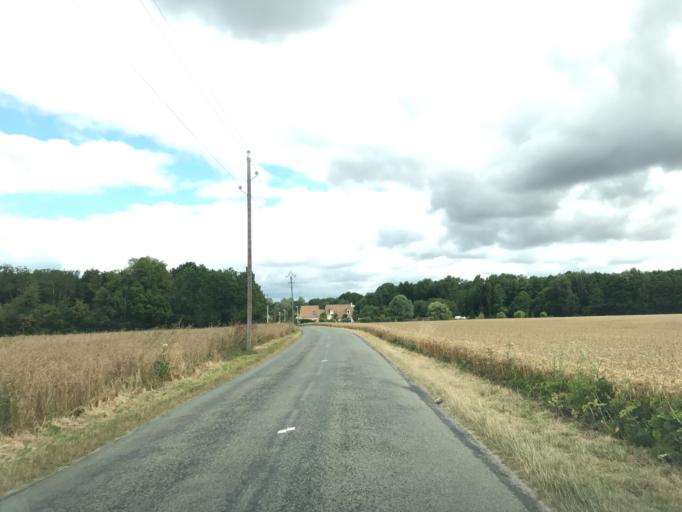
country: FR
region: Haute-Normandie
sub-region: Departement de l'Eure
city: Houlbec-Cocherel
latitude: 49.0593
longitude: 1.2978
